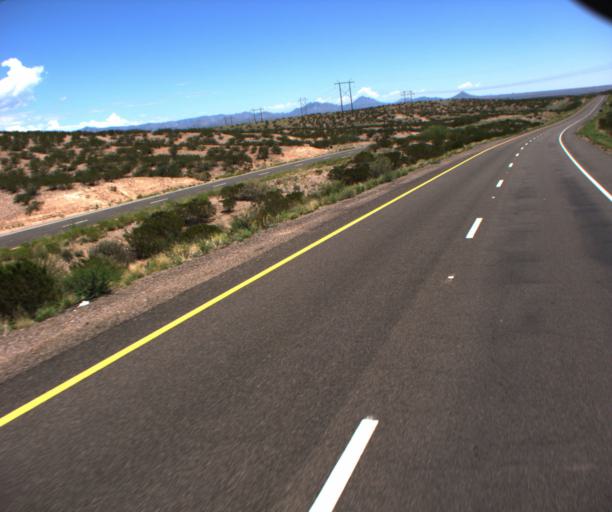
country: US
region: Arizona
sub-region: Greenlee County
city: Clifton
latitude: 32.9905
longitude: -109.2693
